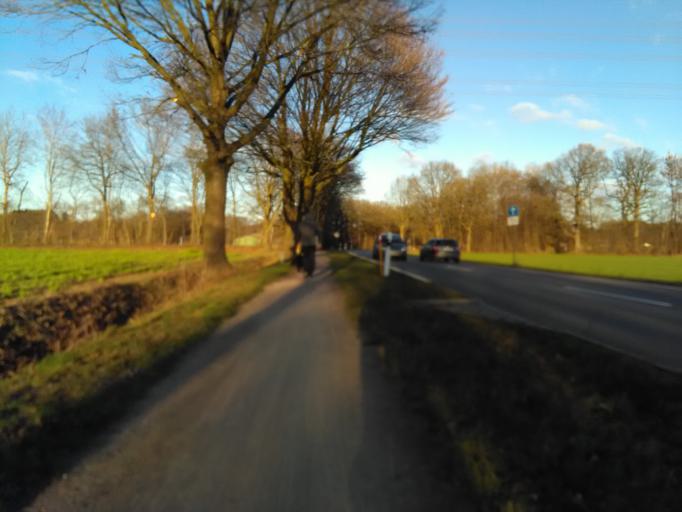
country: DE
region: Schleswig-Holstein
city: Ellerau
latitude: 53.7444
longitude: 9.9100
